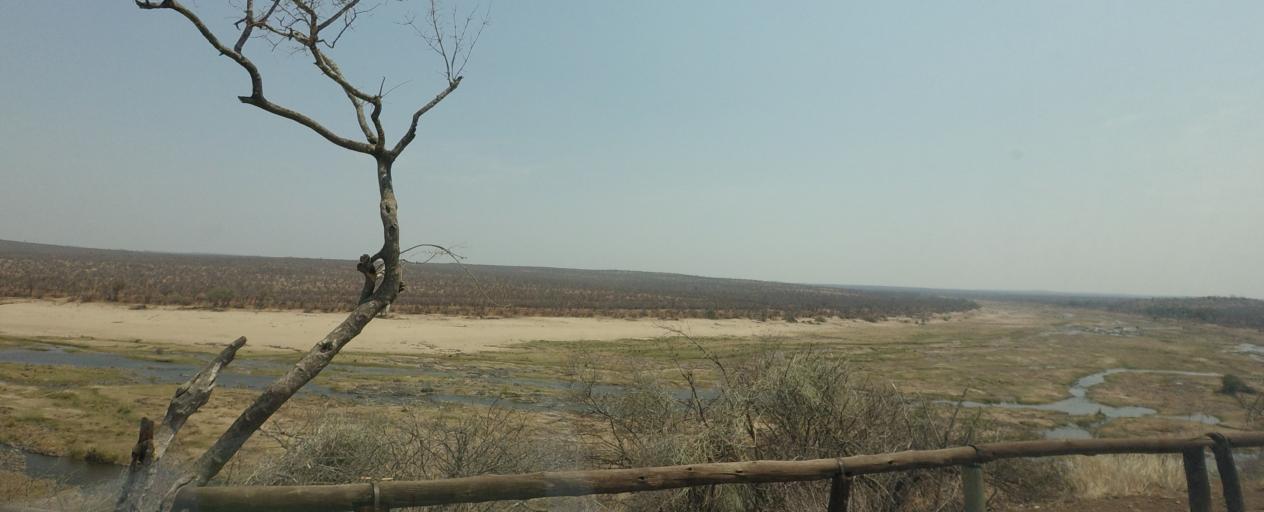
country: ZA
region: Limpopo
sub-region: Mopani District Municipality
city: Phalaborwa
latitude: -24.0172
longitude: 31.6676
